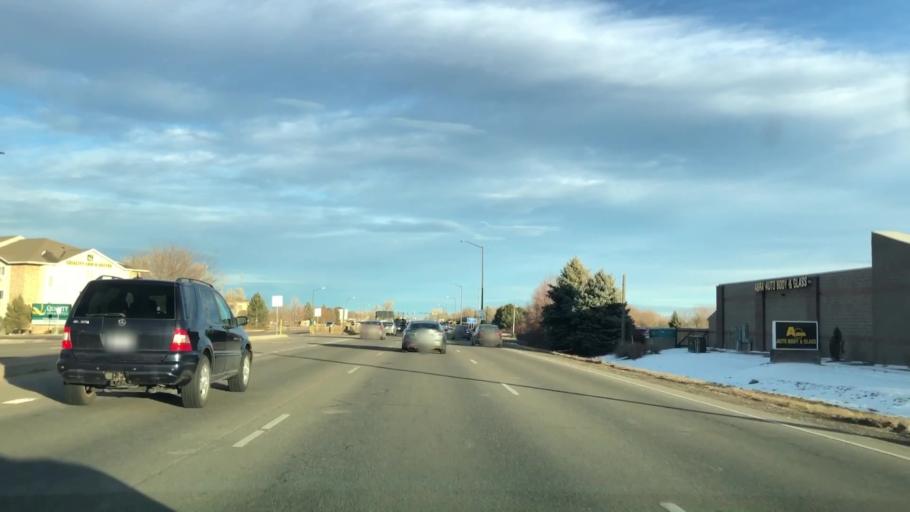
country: US
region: Colorado
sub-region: Larimer County
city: Loveland
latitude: 40.4071
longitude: -105.0514
